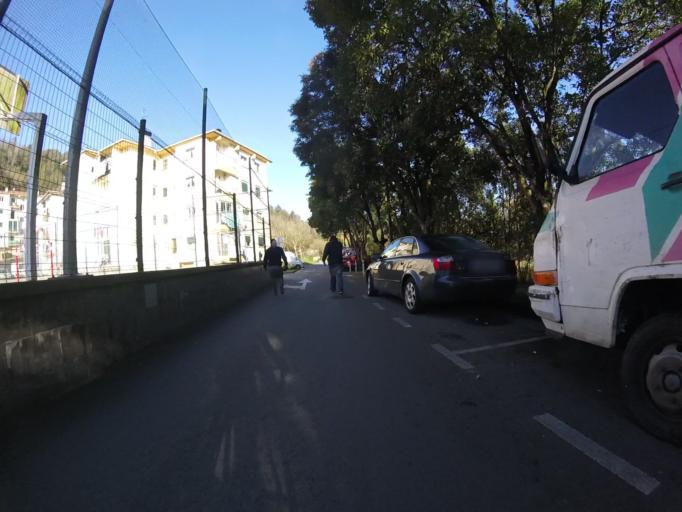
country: ES
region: Basque Country
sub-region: Provincia de Guipuzcoa
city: Usurbil
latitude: 43.2673
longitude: -2.0567
